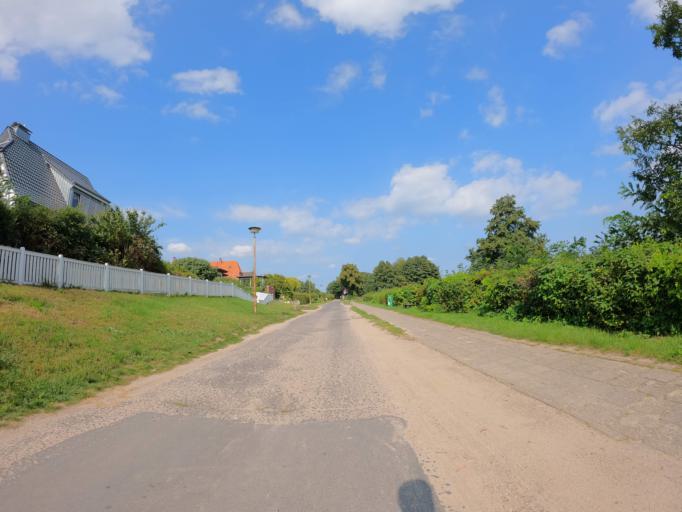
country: DE
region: Mecklenburg-Vorpommern
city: Malchow
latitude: 53.4821
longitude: 12.4376
